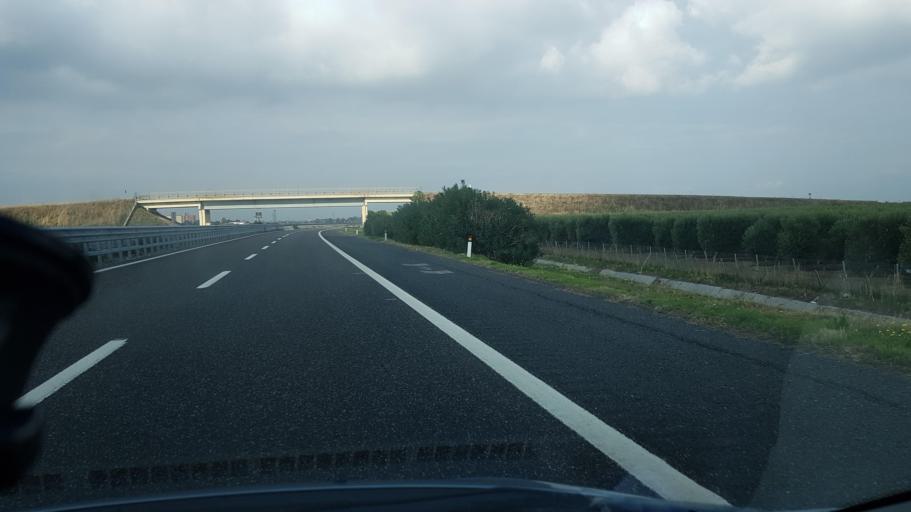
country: IT
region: Apulia
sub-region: Provincia di Foggia
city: Carapelle
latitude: 41.3998
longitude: 15.6809
